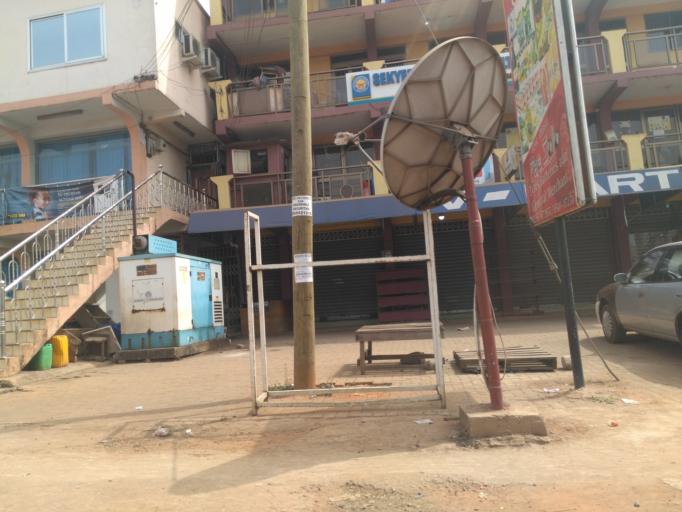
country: GH
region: Ashanti
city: Kumasi
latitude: 6.7067
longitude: -1.6394
